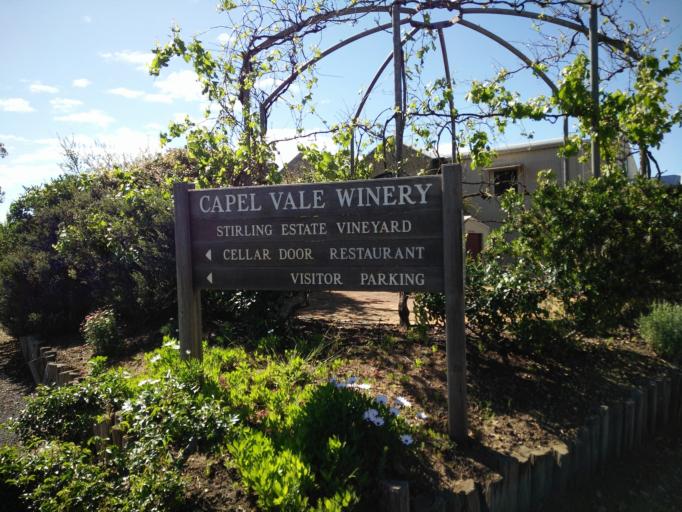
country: AU
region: Western Australia
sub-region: Capel
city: Capel
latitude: -33.5416
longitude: 115.5502
